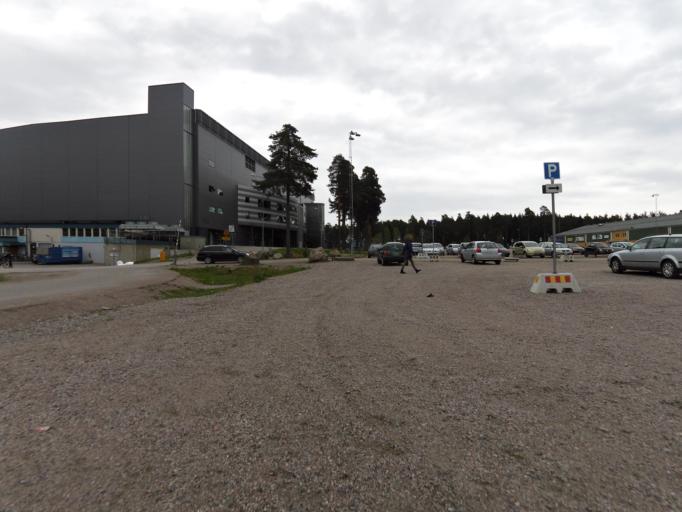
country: SE
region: Gaevleborg
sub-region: Gavle Kommun
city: Gavle
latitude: 60.6915
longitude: 17.1302
